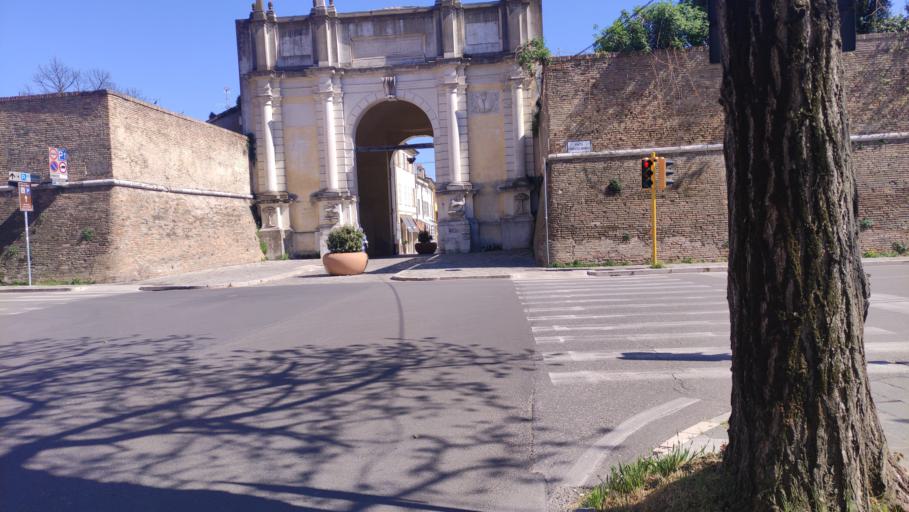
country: IT
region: Emilia-Romagna
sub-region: Provincia di Ravenna
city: Ravenna
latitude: 44.4198
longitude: 12.1939
